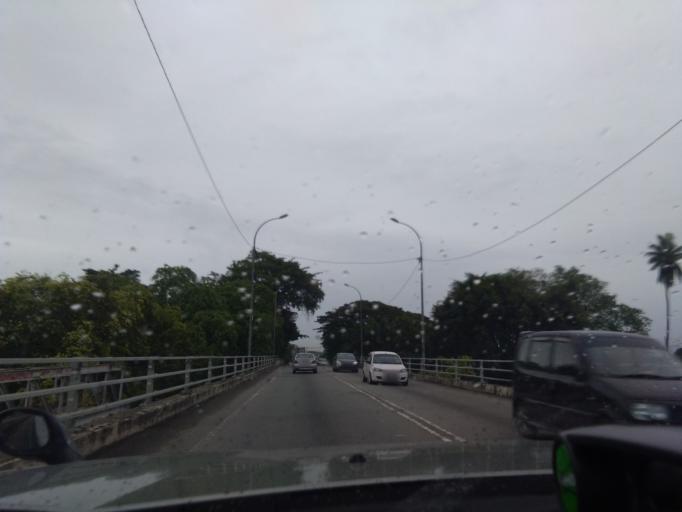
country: MY
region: Penang
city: Nibong Tebal
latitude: 5.1643
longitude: 100.4789
